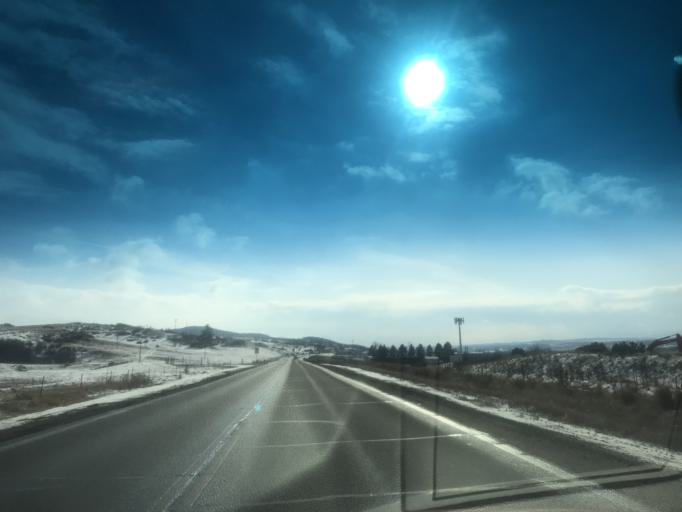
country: US
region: Colorado
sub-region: Douglas County
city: Highlands Ranch
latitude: 39.4748
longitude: -104.9907
